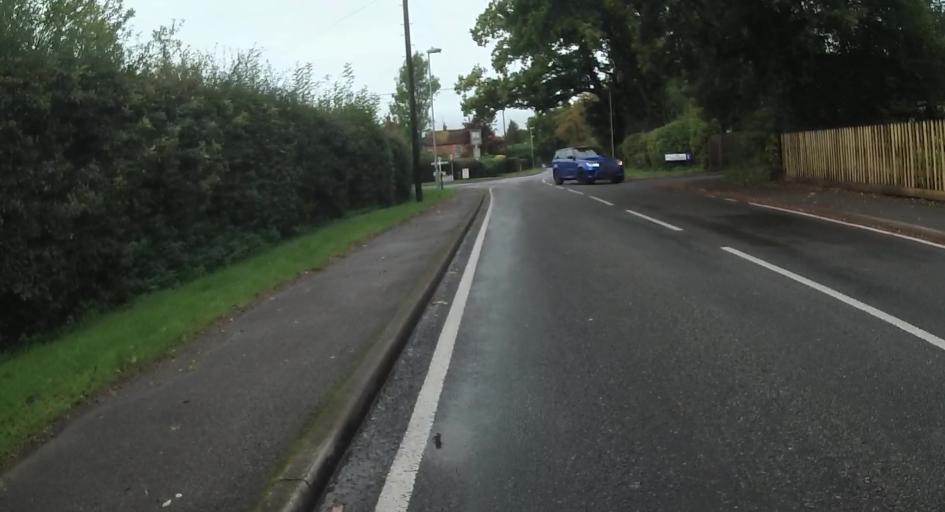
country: GB
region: England
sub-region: Hampshire
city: Tadley
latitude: 51.3523
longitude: -1.1683
